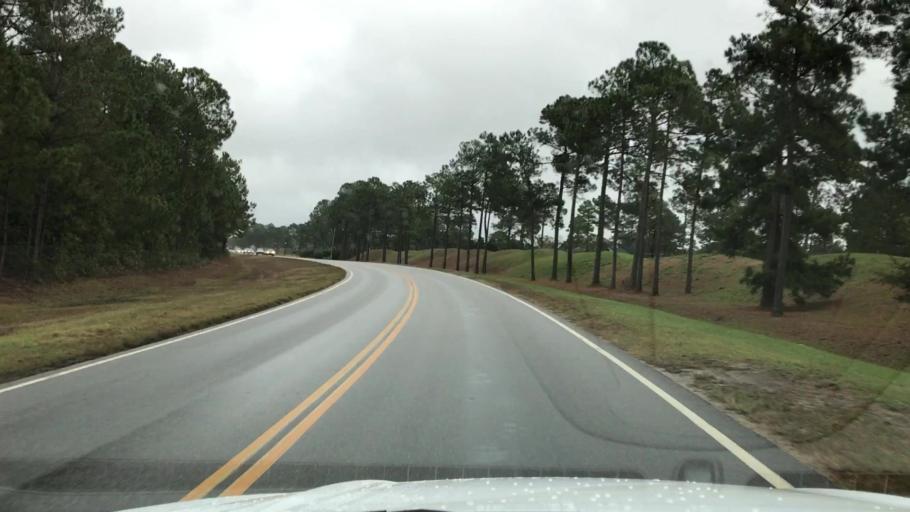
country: US
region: South Carolina
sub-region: Horry County
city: Forestbrook
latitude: 33.7568
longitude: -78.9130
